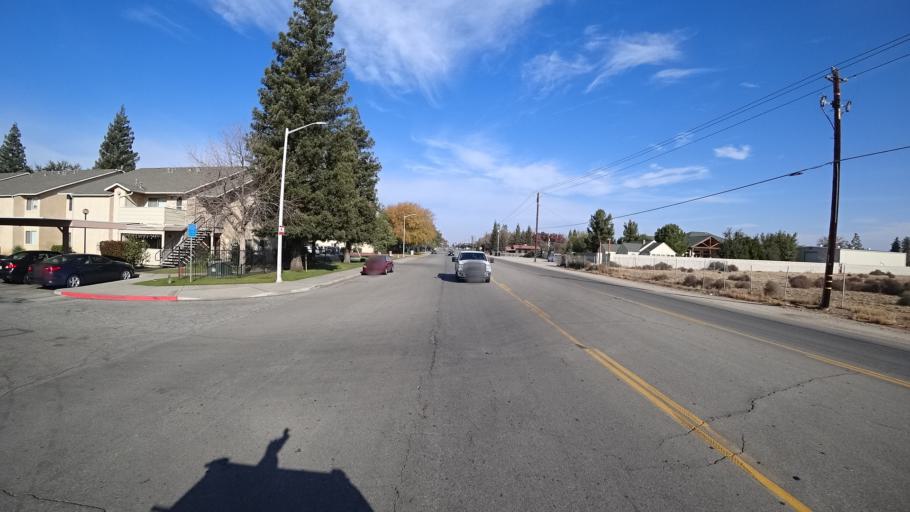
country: US
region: California
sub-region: Kern County
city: Greenacres
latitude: 35.3984
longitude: -119.0744
